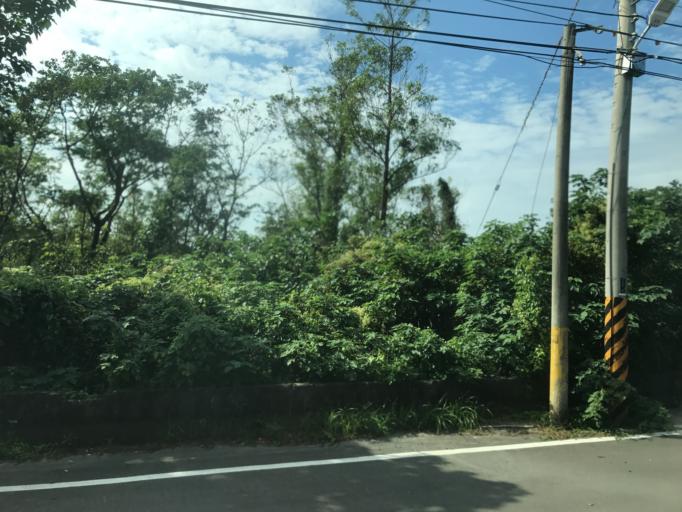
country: TW
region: Taiwan
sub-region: Hsinchu
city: Hsinchu
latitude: 24.7611
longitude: 120.9497
